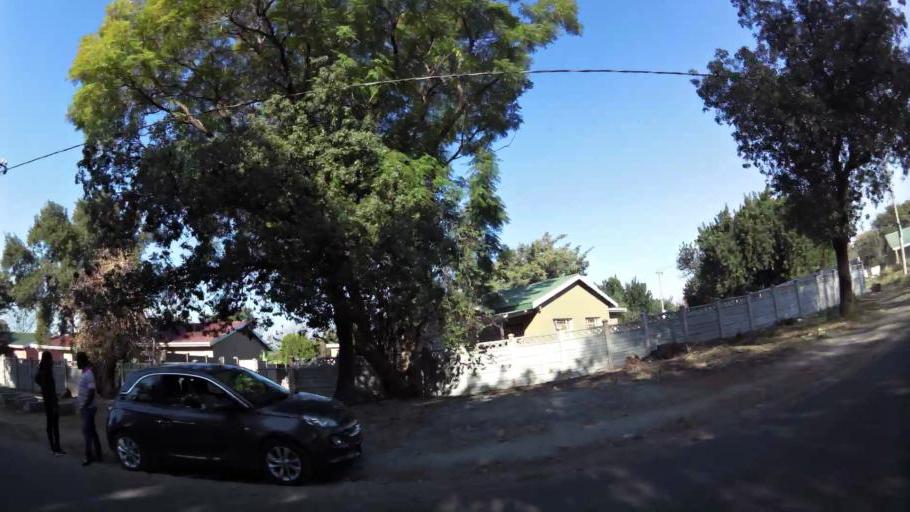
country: ZA
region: North-West
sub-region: Bojanala Platinum District Municipality
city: Rustenburg
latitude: -25.6537
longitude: 27.2380
